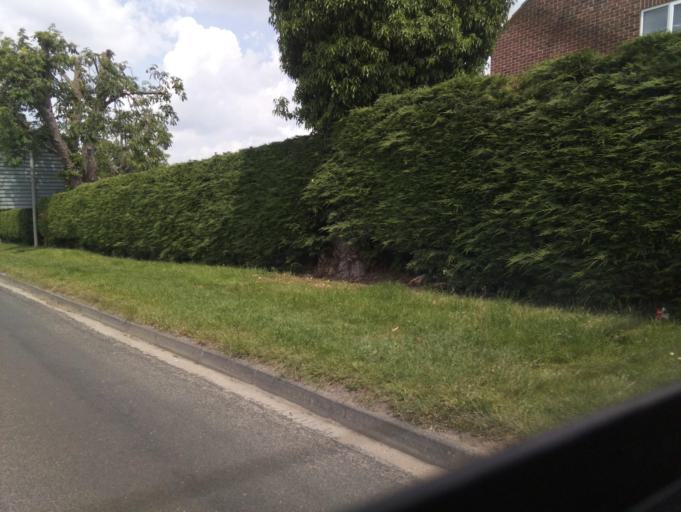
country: GB
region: England
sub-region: North Yorkshire
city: Boroughbridge
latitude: 54.0839
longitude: -1.3956
